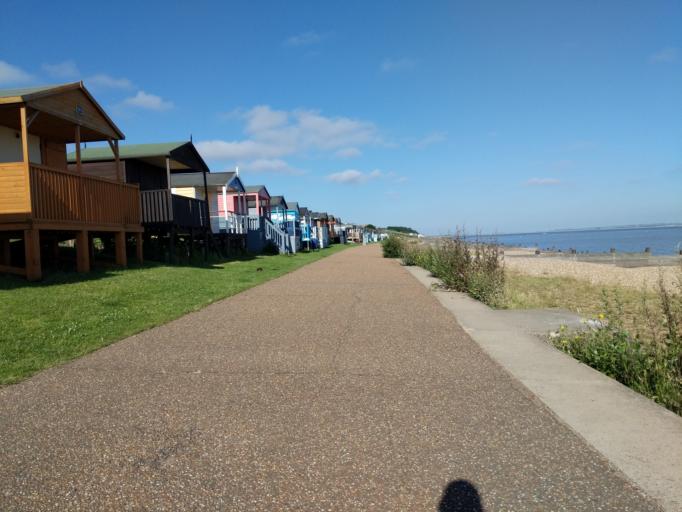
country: GB
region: England
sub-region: Kent
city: Tankerton
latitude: 51.3654
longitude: 1.0539
